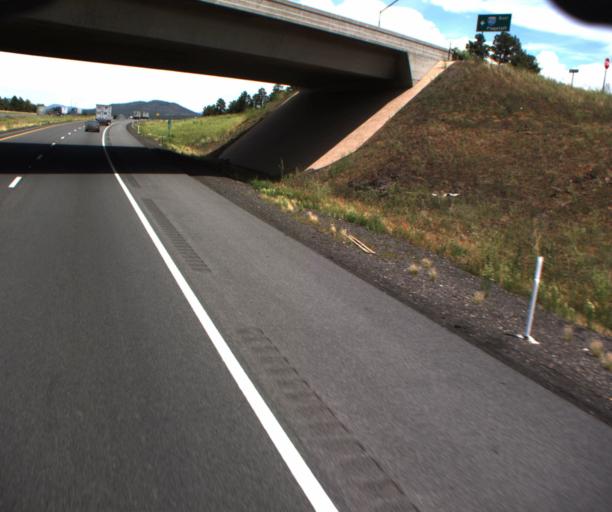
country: US
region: Arizona
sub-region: Coconino County
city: Williams
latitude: 35.2449
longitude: -112.2147
